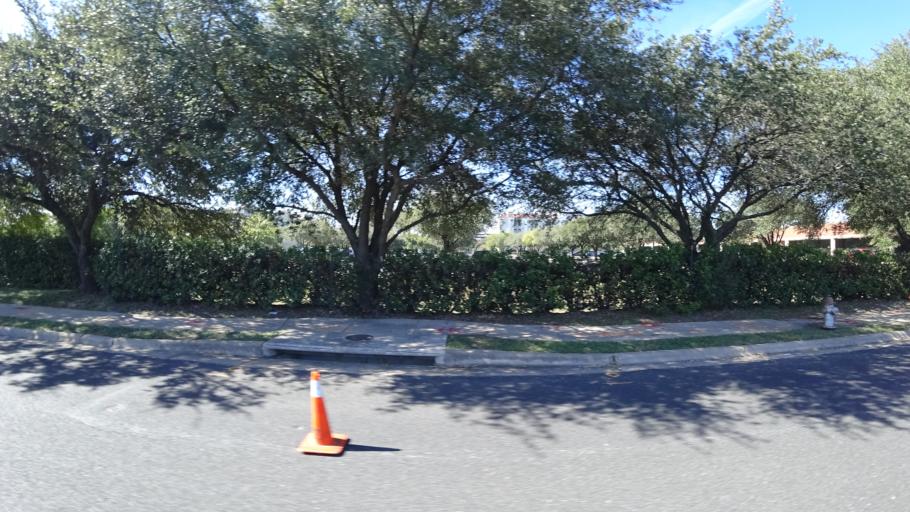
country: US
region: Texas
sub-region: Travis County
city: Austin
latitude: 30.2137
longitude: -97.7475
